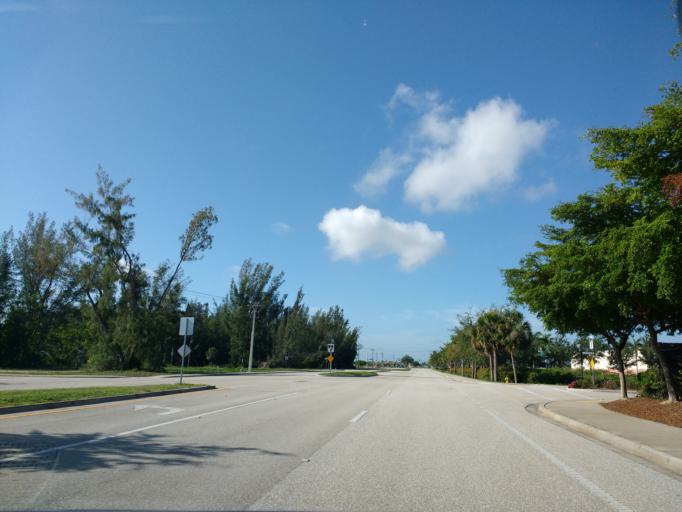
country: US
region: Florida
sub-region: Lee County
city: Cape Coral
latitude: 26.6112
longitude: -82.0235
